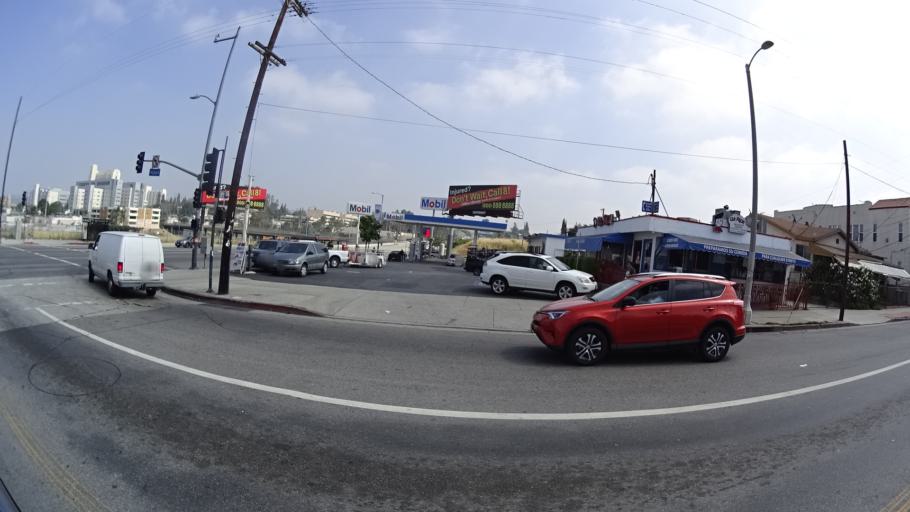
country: US
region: California
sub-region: Los Angeles County
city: Boyle Heights
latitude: 34.0529
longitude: -118.2036
